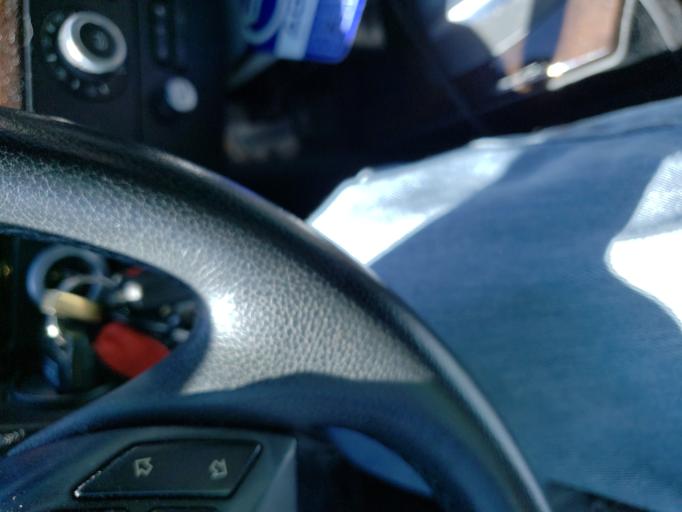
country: US
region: Arizona
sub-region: Maricopa County
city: Paradise Valley
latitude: 33.6169
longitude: -111.9570
